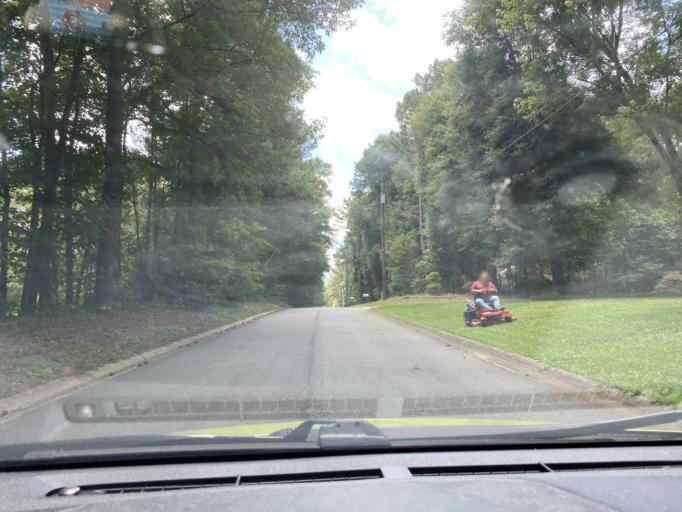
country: US
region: Georgia
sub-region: Fulton County
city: Palmetto
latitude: 33.4364
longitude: -84.6807
